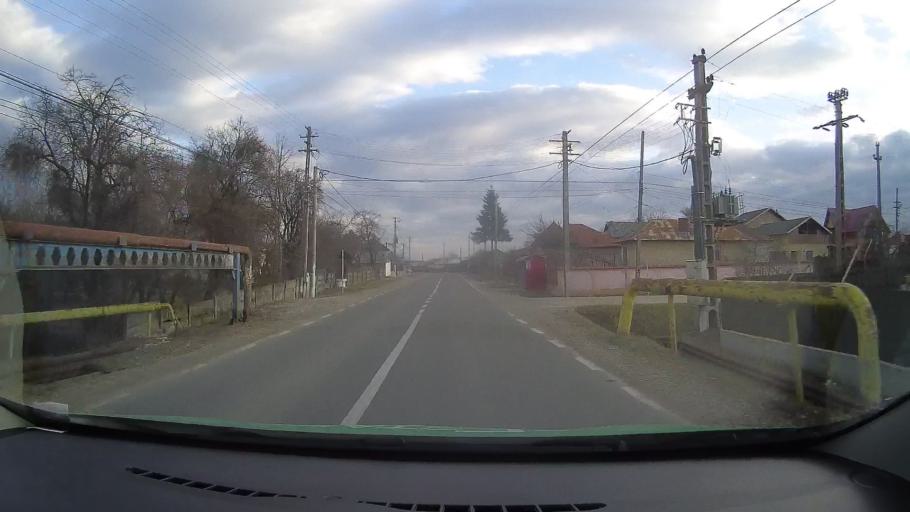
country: RO
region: Dambovita
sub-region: Comuna I. L. Caragiale
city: Ghirdoveni
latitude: 44.9333
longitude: 25.6853
